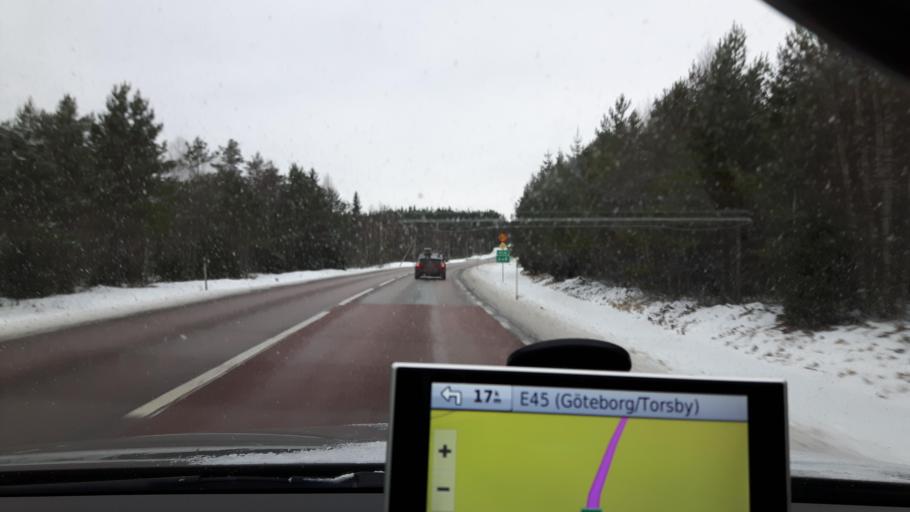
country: SE
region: Vaermland
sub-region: Hagfors Kommun
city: Ekshaerad
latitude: 60.3874
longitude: 13.2562
